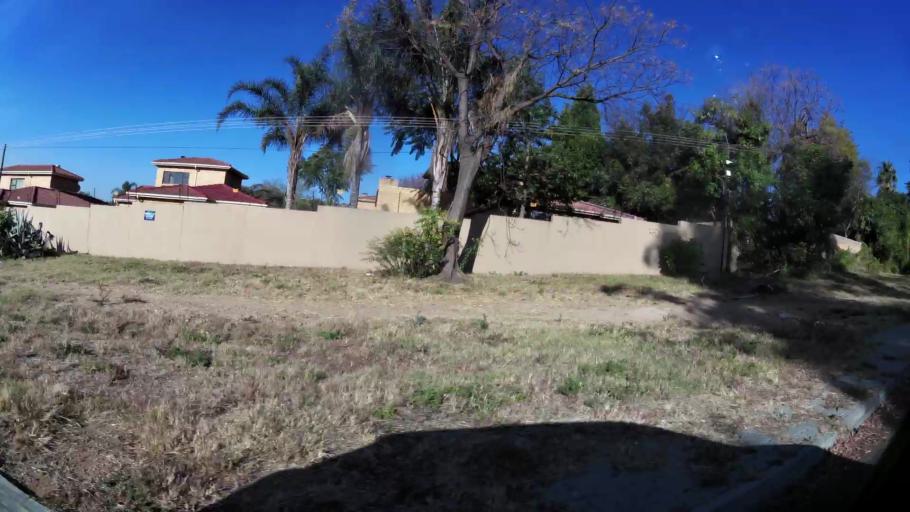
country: ZA
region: Gauteng
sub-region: City of Johannesburg Metropolitan Municipality
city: Roodepoort
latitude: -26.0868
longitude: 27.9472
